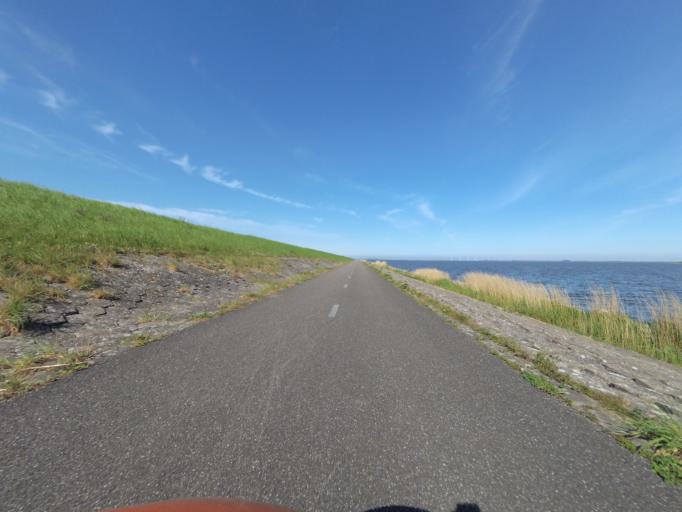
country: NL
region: Flevoland
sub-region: Gemeente Dronten
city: Dronten
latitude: 52.5833
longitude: 5.7458
